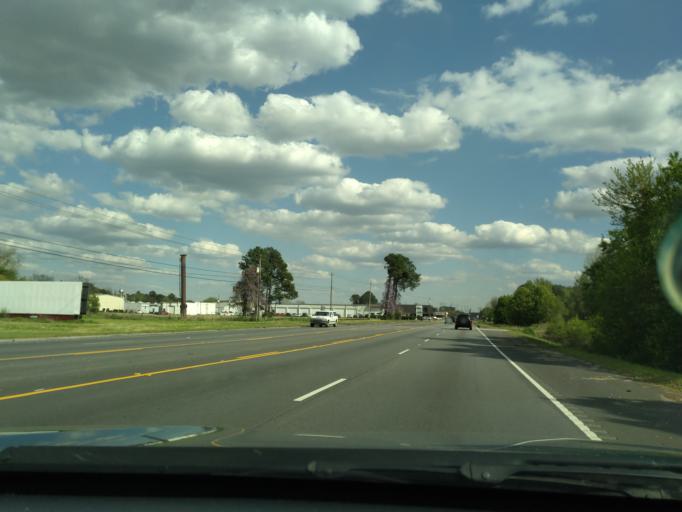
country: US
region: South Carolina
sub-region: Florence County
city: Florence
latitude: 34.2147
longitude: -79.7808
